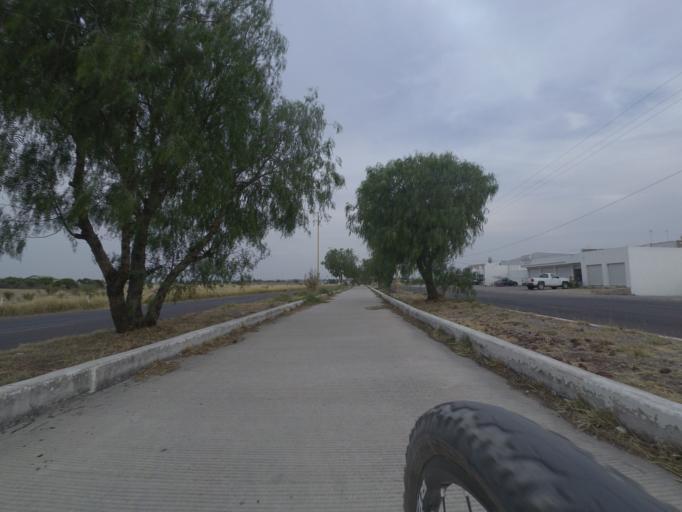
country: MX
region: Aguascalientes
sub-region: Aguascalientes
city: La Loma de los Negritos
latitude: 21.8603
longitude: -102.3661
